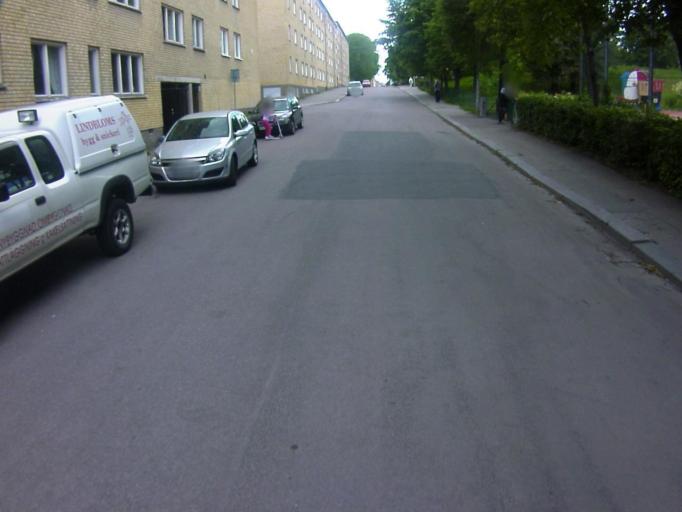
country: SE
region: Soedermanland
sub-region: Eskilstuna Kommun
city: Eskilstuna
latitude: 59.3675
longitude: 16.5091
